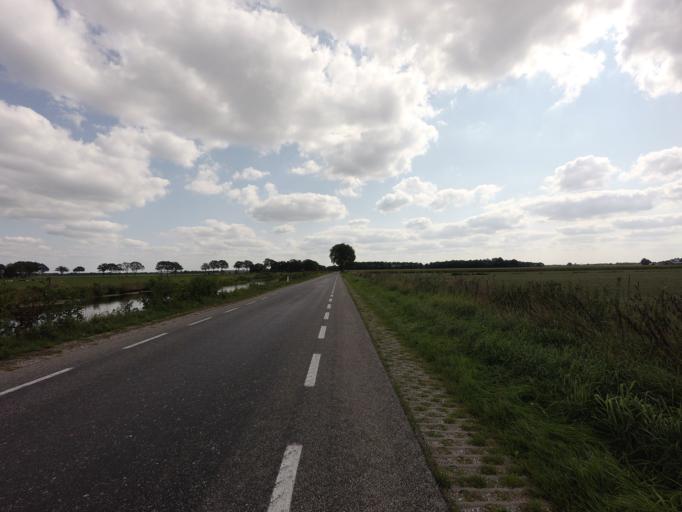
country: NL
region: Drenthe
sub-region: Gemeente Westerveld
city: Dwingeloo
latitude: 52.8783
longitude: 6.4306
